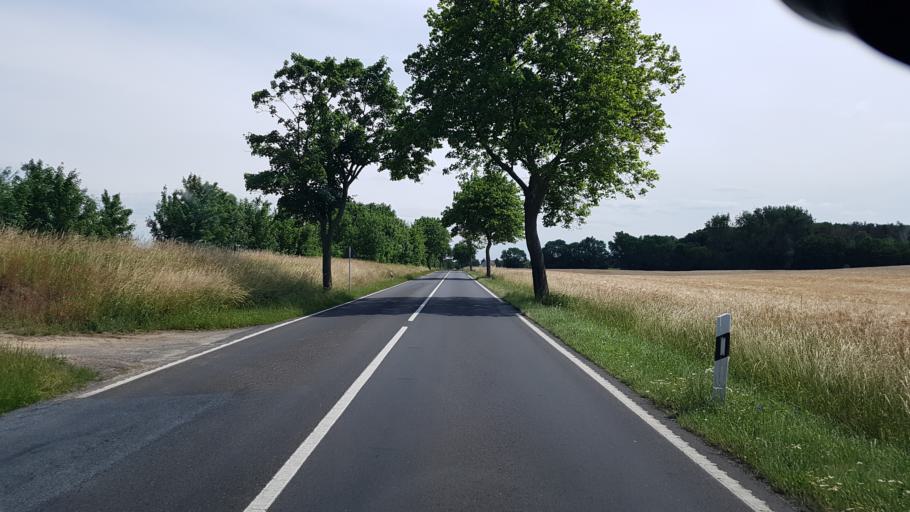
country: DE
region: Brandenburg
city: Prenzlau
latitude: 53.3919
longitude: 13.7710
